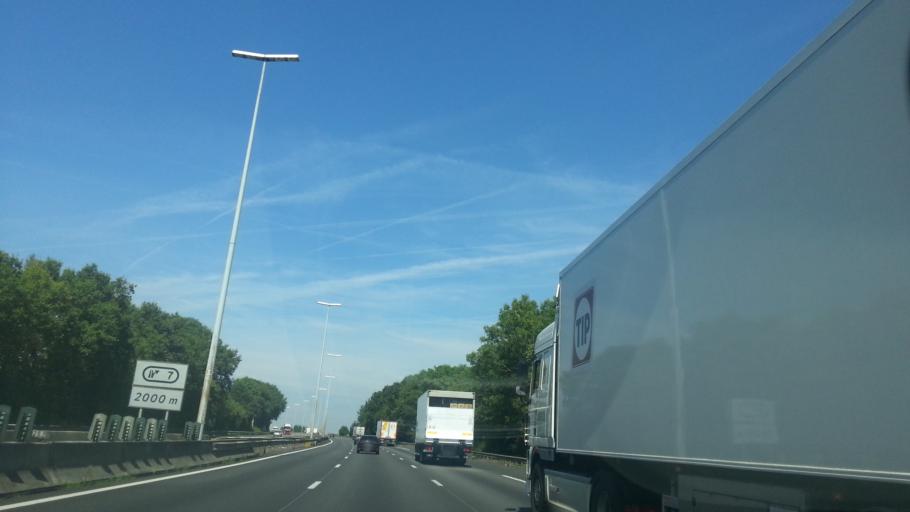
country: FR
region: Ile-de-France
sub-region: Departement du Val-d'Oise
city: Vemars
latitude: 49.0622
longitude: 2.5521
